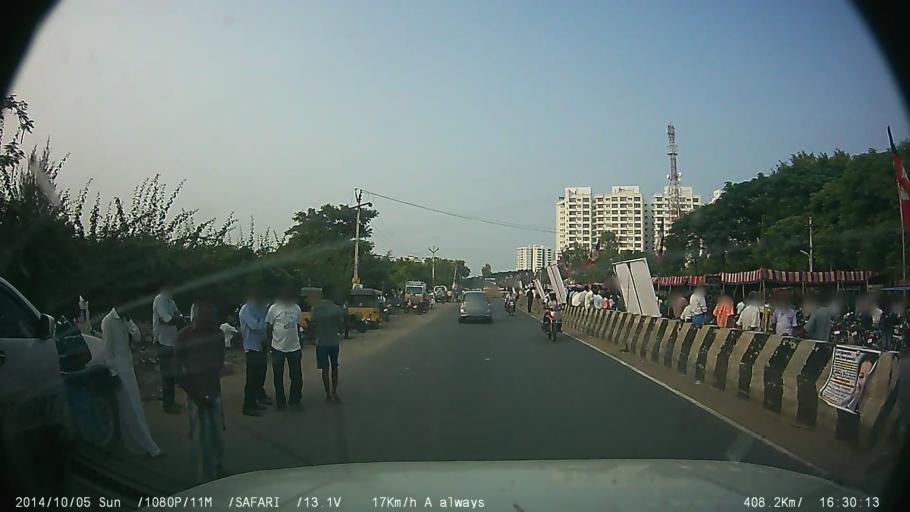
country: IN
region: Tamil Nadu
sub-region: Kancheepuram
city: Vengavasal
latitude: 12.7902
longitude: 80.2217
